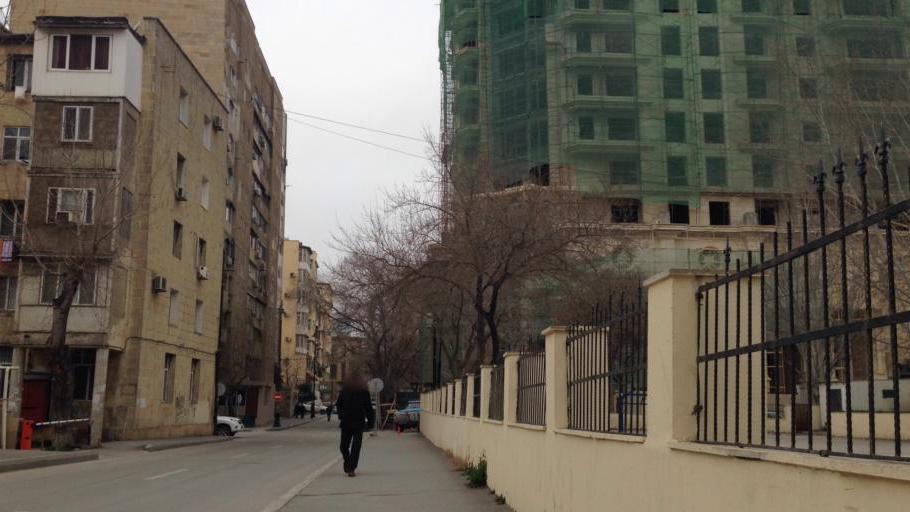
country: AZ
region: Baki
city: Badamdar
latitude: 40.3787
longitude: 49.8392
